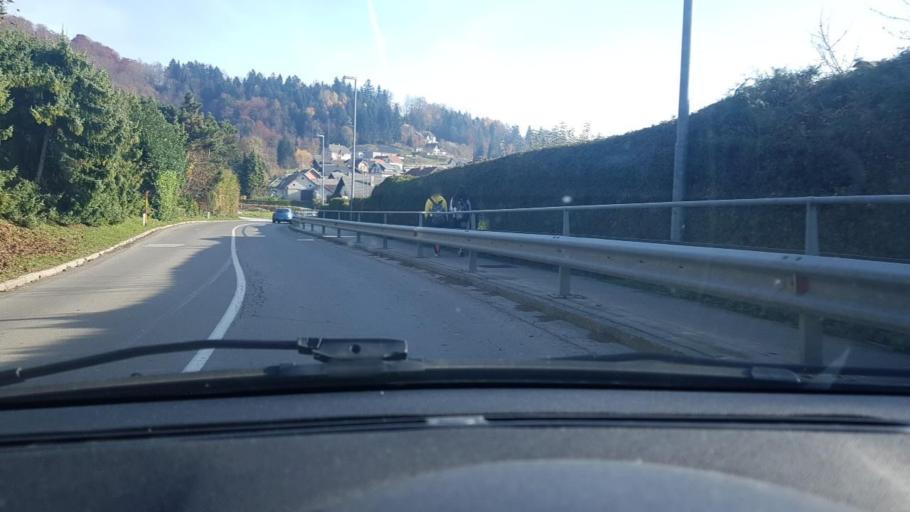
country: SI
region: Trzic
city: Bistrica pri Trzicu
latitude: 46.3387
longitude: 14.3012
